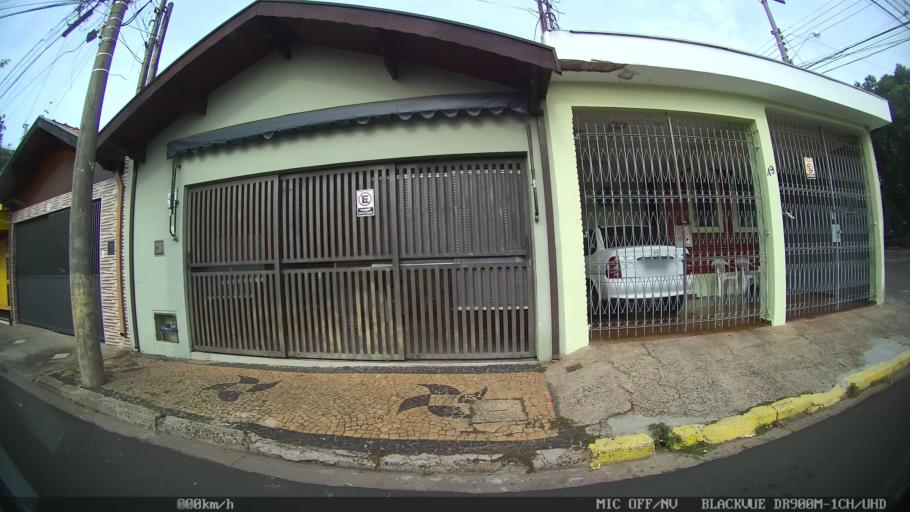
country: BR
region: Sao Paulo
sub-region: Piracicaba
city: Piracicaba
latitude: -22.7395
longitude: -47.6247
